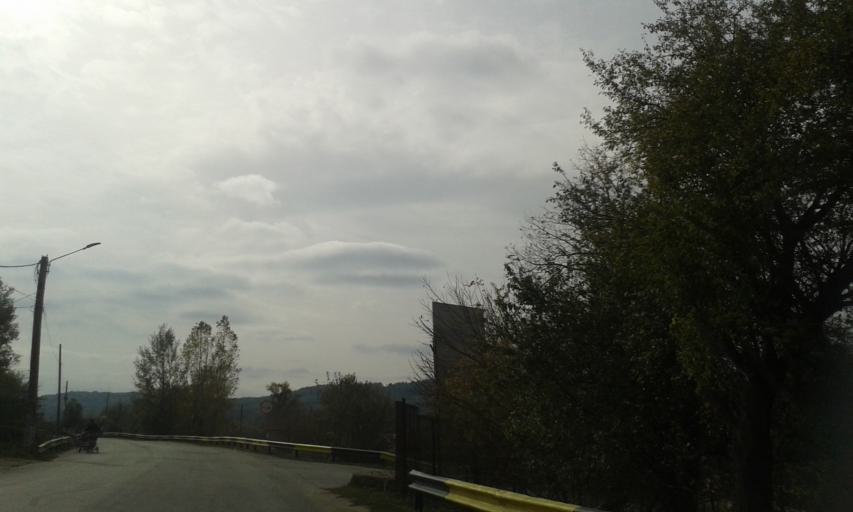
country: RO
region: Gorj
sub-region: Comuna Targu Carbunesti
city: Targu Carbunesti
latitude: 44.9498
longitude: 23.5132
